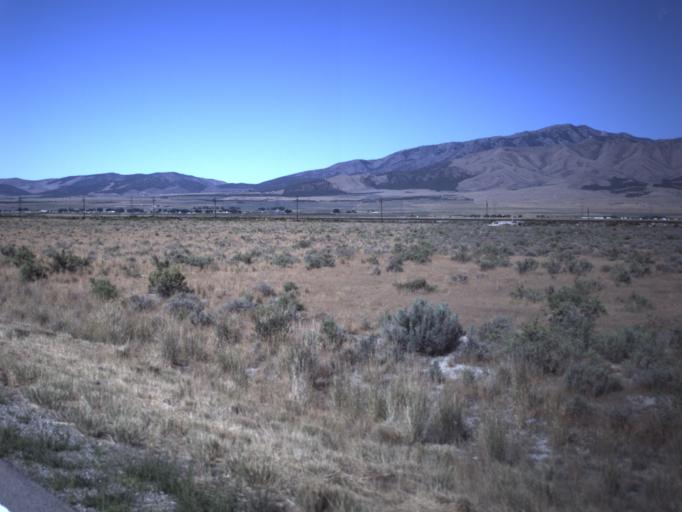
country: US
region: Utah
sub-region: Tooele County
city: Tooele
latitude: 40.3684
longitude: -112.4048
